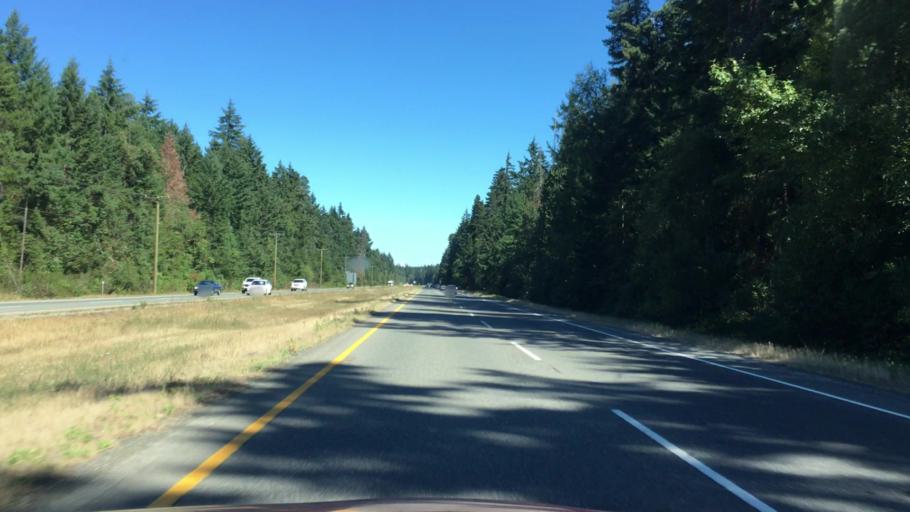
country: CA
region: British Columbia
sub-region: Regional District of Nanaimo
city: Parksville
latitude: 49.3019
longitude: -124.3016
